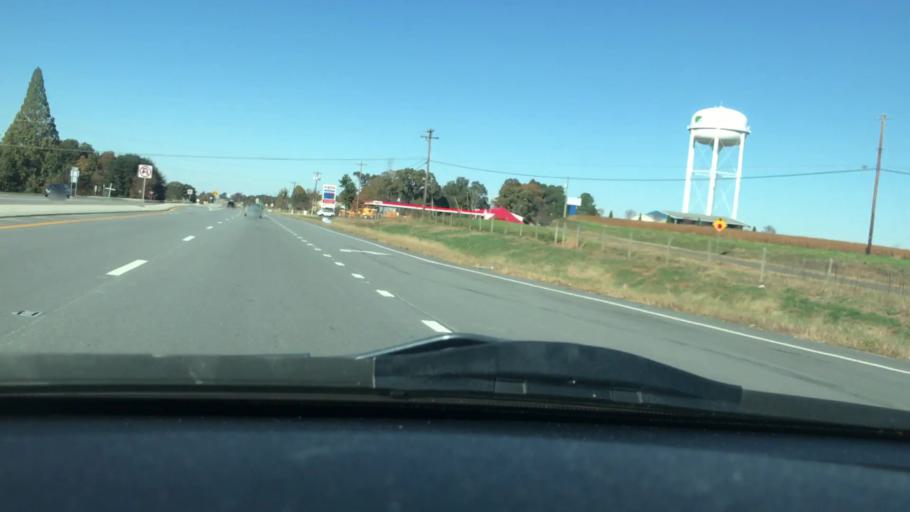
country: US
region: North Carolina
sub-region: Guilford County
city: Stokesdale
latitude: 36.2925
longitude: -79.9400
